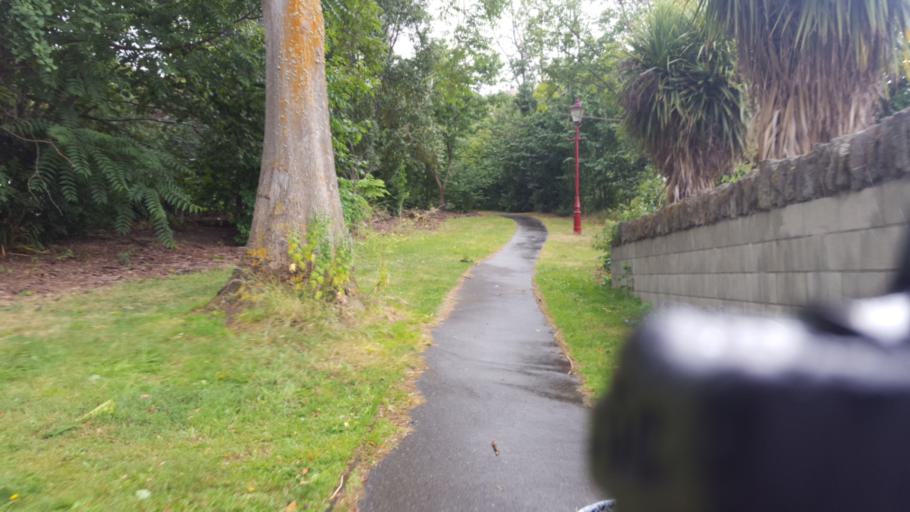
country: NZ
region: Otago
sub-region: Queenstown-Lakes District
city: Wanaka
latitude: -45.1849
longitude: 169.3152
